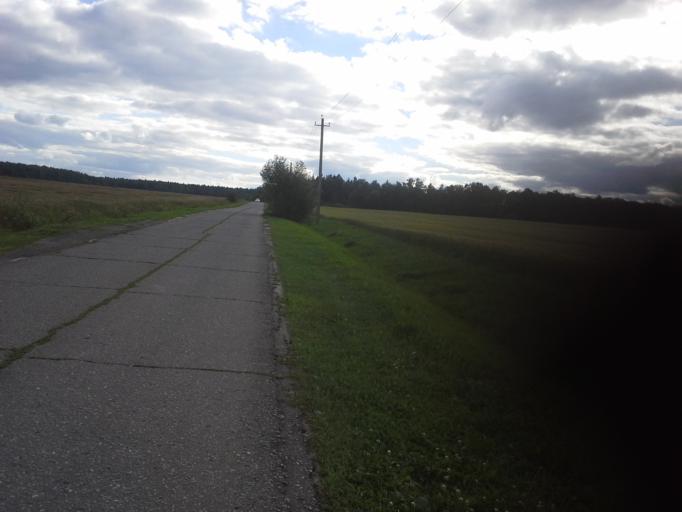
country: RU
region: Moskovskaya
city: Kievskij
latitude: 55.4568
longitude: 36.8768
